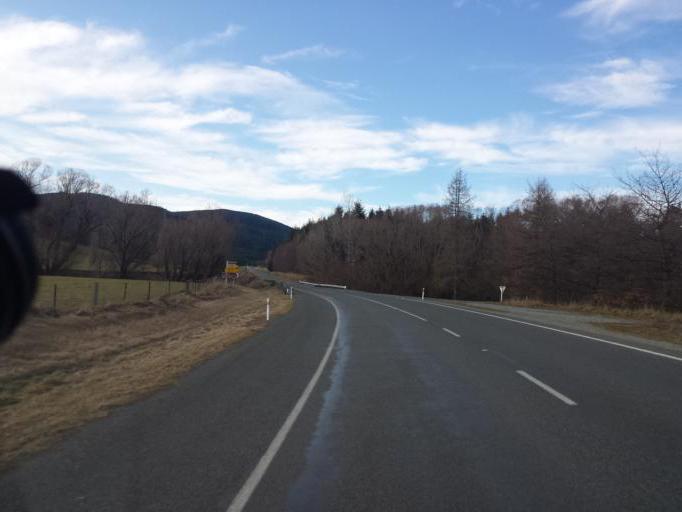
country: NZ
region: Canterbury
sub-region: Timaru District
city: Pleasant Point
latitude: -44.1230
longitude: 171.0451
